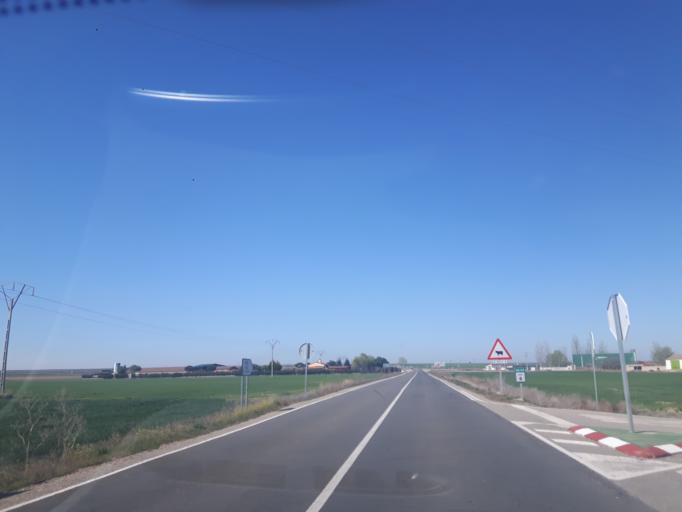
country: ES
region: Castille and Leon
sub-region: Provincia de Salamanca
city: Nava de Sotrobal
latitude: 40.8875
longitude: -5.2820
